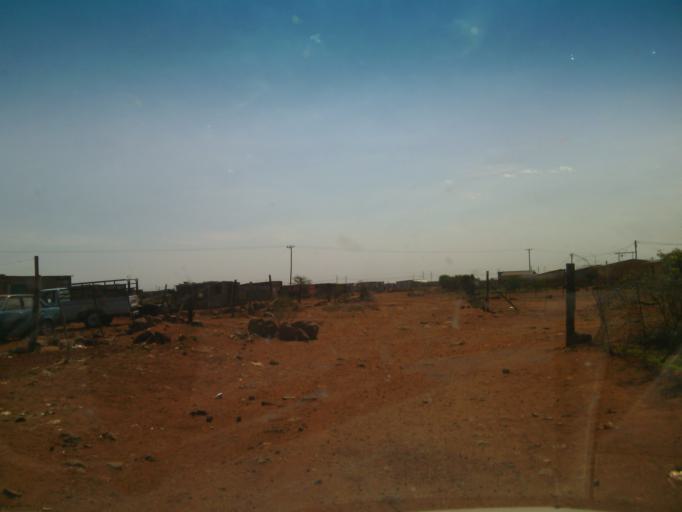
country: ZA
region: Northern Cape
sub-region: Frances Baard District Municipality
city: Barkly West
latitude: -28.5206
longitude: 24.4994
